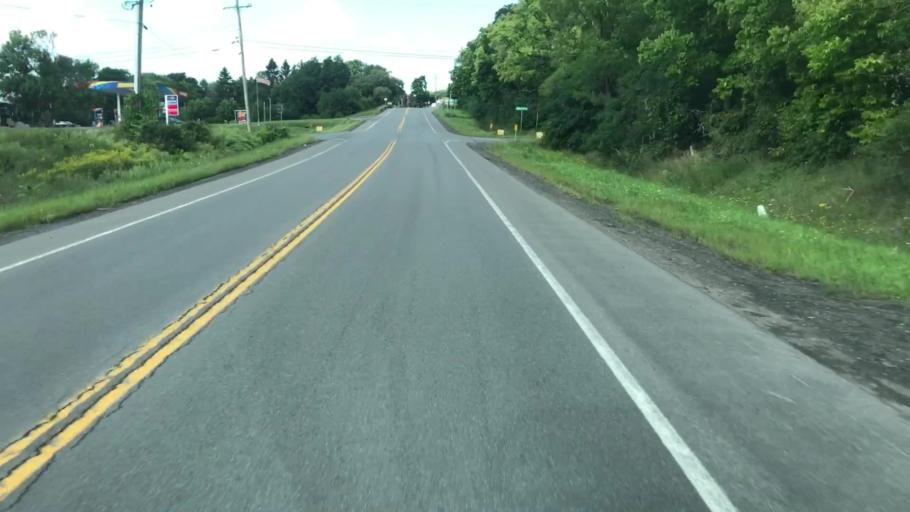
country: US
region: New York
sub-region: Onondaga County
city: Marcellus
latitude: 42.9794
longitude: -76.3311
